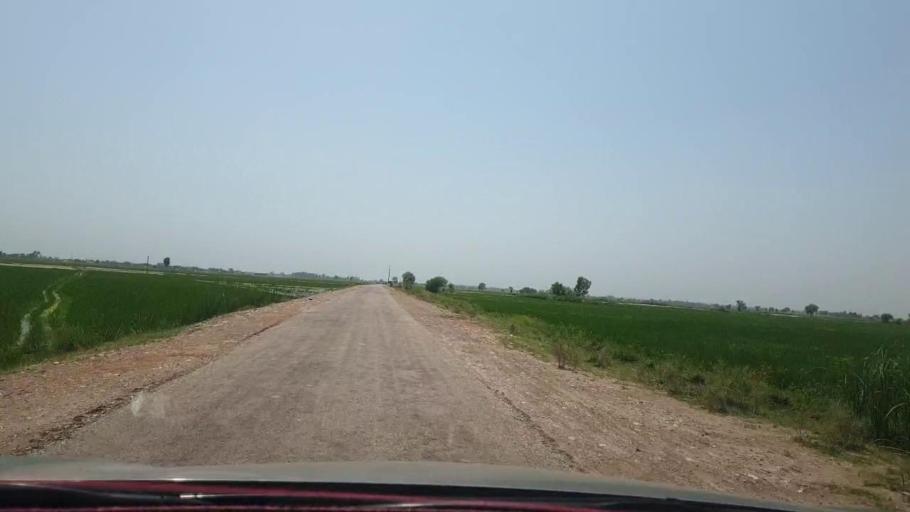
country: PK
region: Sindh
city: Warah
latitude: 27.5574
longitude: 67.7987
